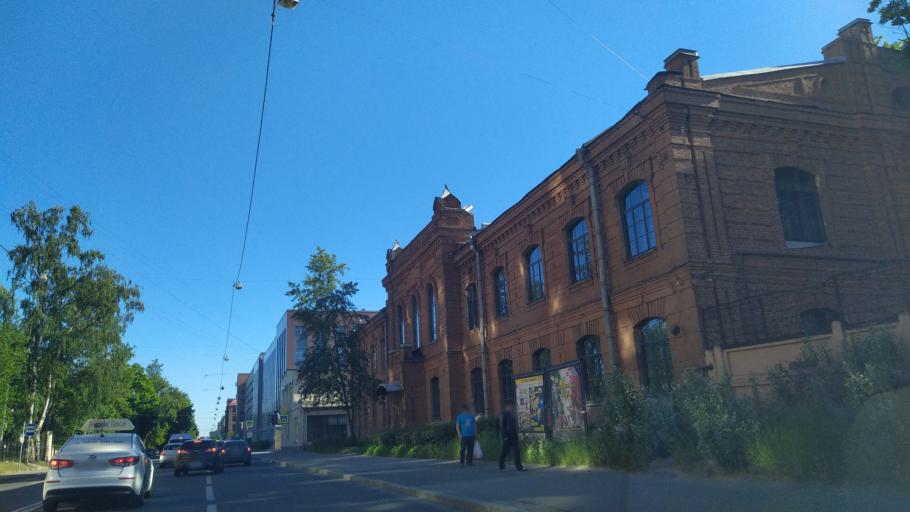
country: RU
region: Leningrad
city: Sampsonievskiy
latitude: 59.9778
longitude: 30.3379
